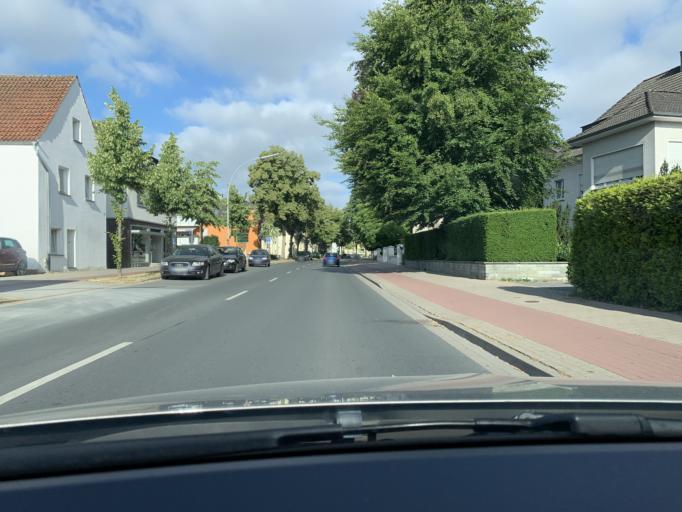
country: DE
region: North Rhine-Westphalia
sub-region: Regierungsbezirk Detmold
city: Rheda-Wiedenbruck
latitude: 51.8554
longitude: 8.2917
